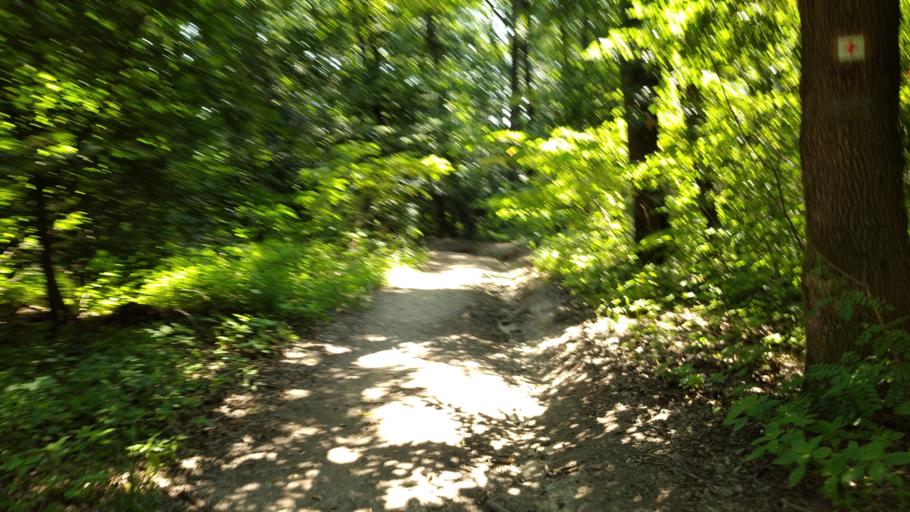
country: HU
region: Nograd
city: Nagyoroszi
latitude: 48.0243
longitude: 19.0413
